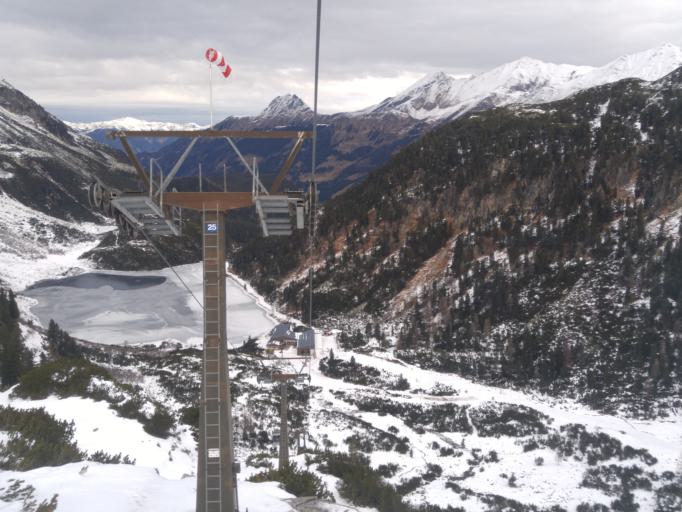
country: AT
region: Salzburg
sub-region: Politischer Bezirk Zell am See
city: Niedernsill
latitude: 47.1503
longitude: 12.6244
